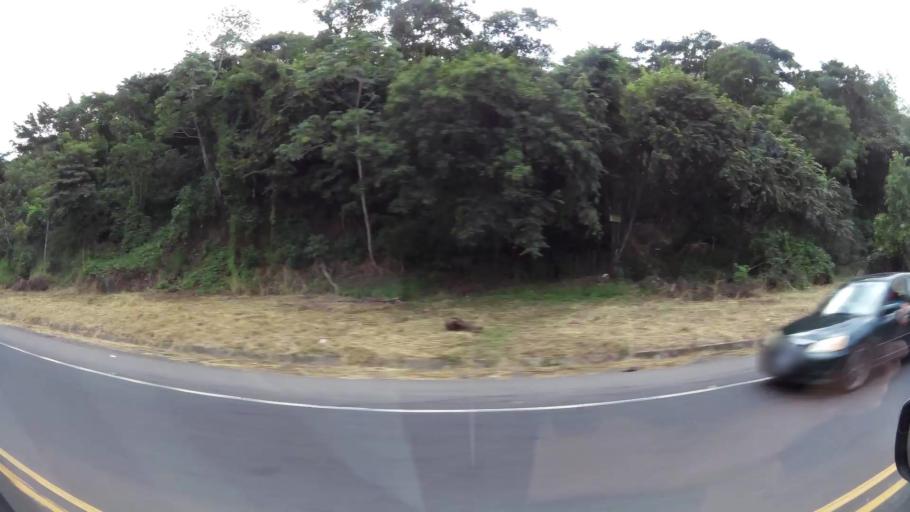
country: CR
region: Puntarenas
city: Esparza
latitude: 9.9184
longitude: -84.7053
